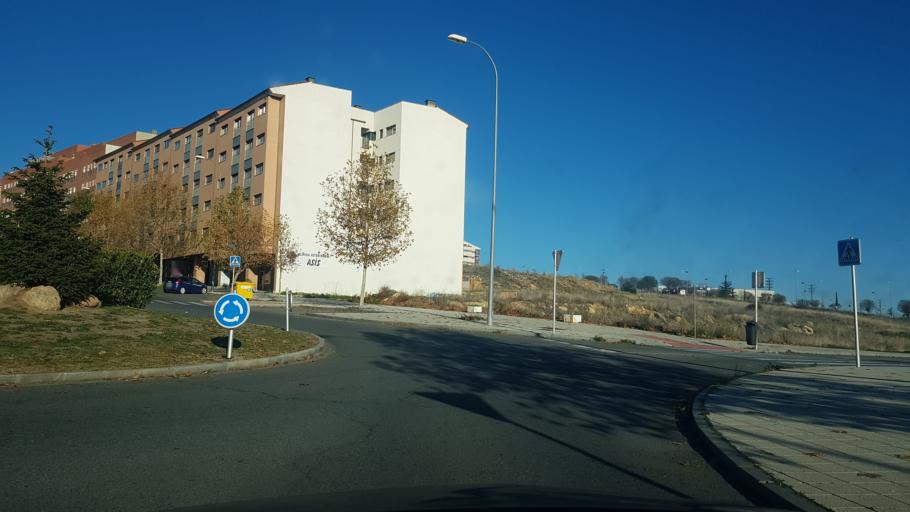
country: ES
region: Castille and Leon
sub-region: Provincia de Avila
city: Avila
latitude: 40.6468
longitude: -4.6781
